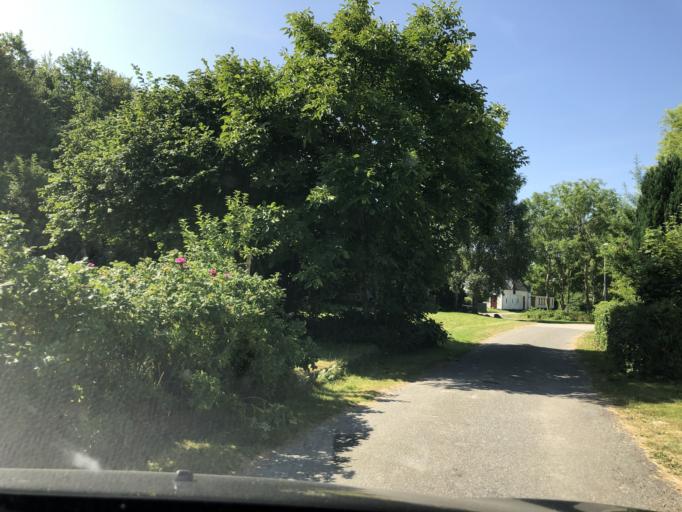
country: DK
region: South Denmark
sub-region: Faaborg-Midtfyn Kommune
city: Faaborg
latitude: 54.9568
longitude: 10.2261
